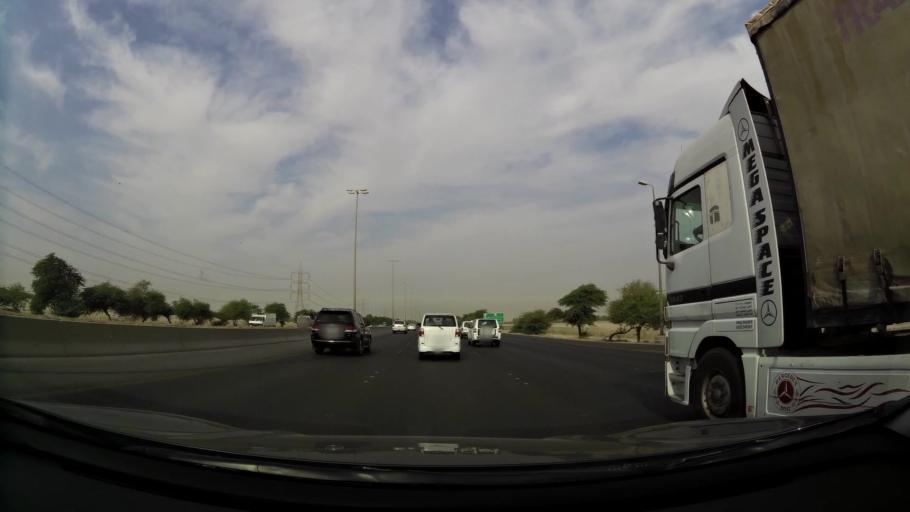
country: KW
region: Al Asimah
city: Ar Rabiyah
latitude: 29.2698
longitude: 47.8227
